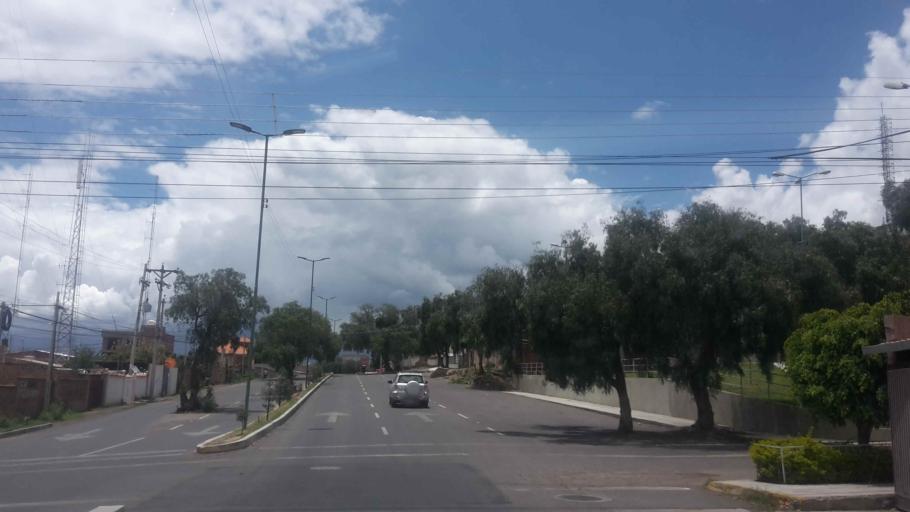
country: BO
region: Cochabamba
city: Cochabamba
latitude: -17.3552
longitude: -66.1560
